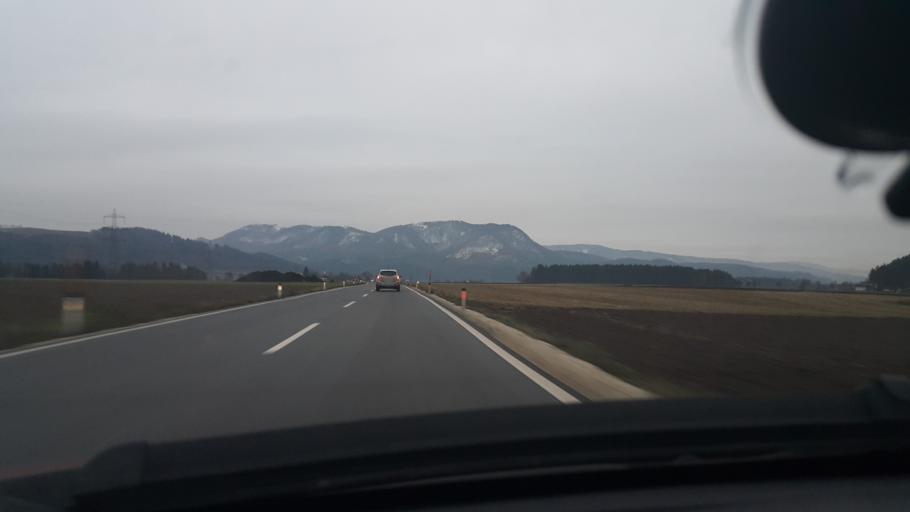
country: AT
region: Carinthia
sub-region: Politischer Bezirk Volkermarkt
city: Griffen
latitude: 46.6921
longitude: 14.7394
